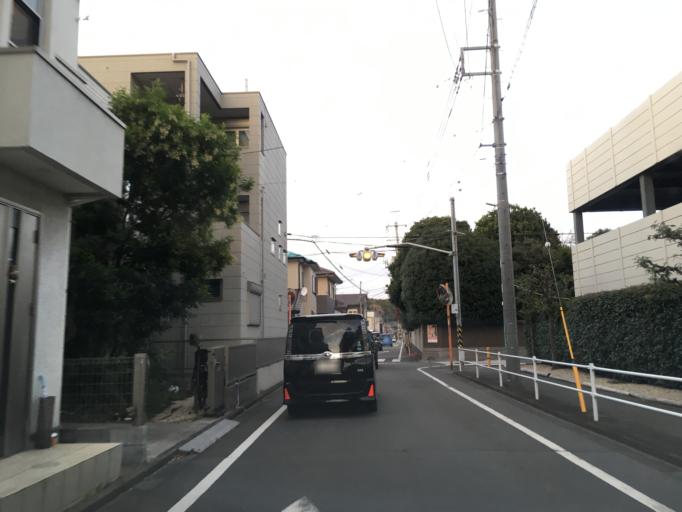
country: JP
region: Tokyo
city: Hachioji
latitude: 35.5971
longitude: 139.3513
